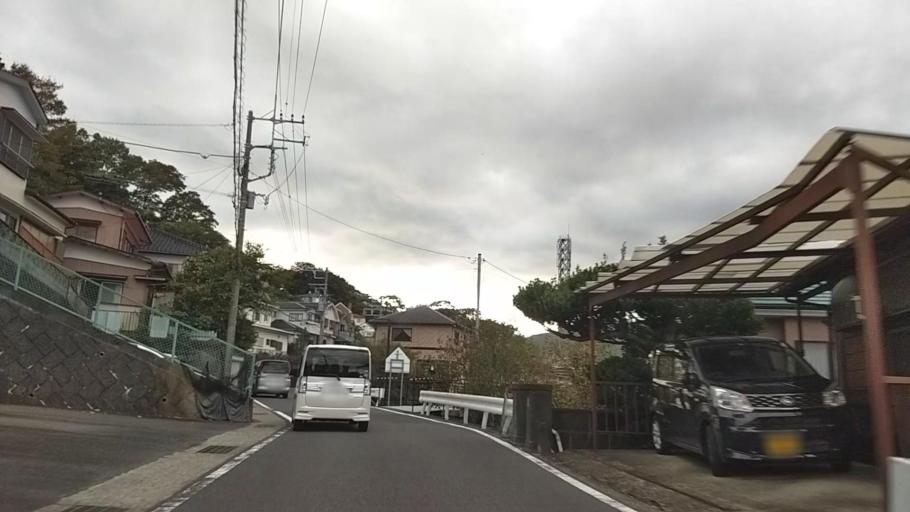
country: JP
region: Kanagawa
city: Yugawara
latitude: 35.1560
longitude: 139.1373
